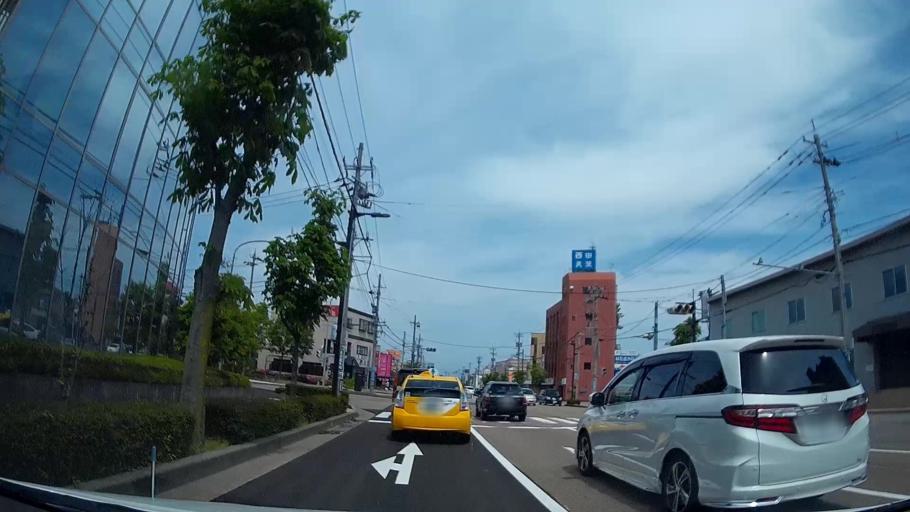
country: JP
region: Ishikawa
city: Kanazawa-shi
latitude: 36.5893
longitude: 136.6469
